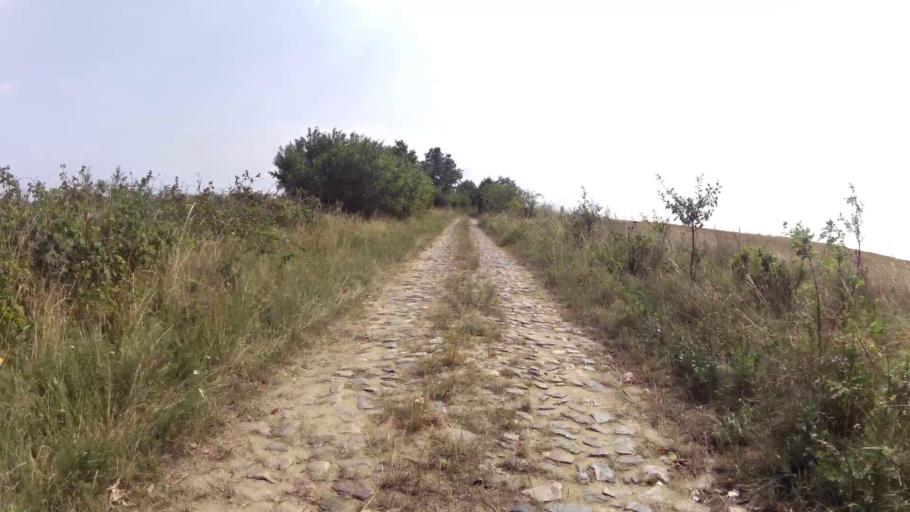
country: PL
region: West Pomeranian Voivodeship
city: Trzcinsko Zdroj
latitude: 52.8966
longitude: 14.5227
